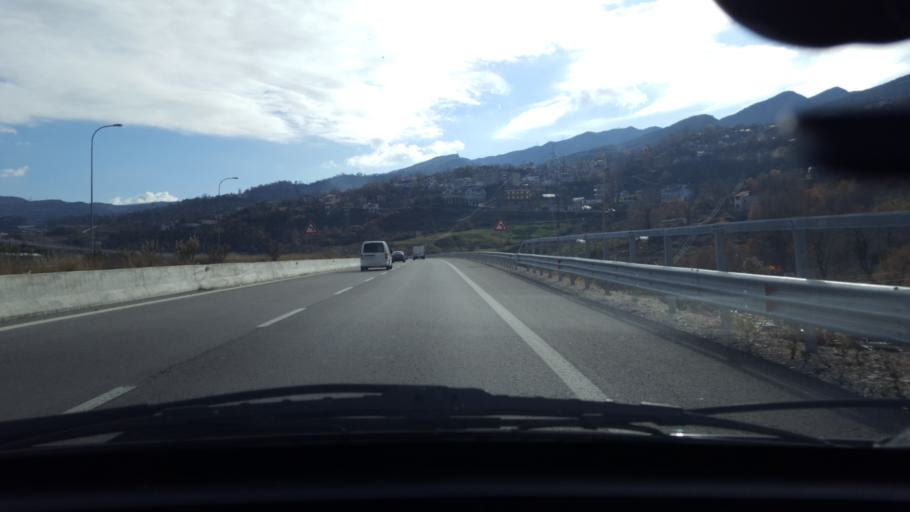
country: AL
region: Tirane
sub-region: Rrethi i Tiranes
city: Berzhite
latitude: 41.2304
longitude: 19.9293
